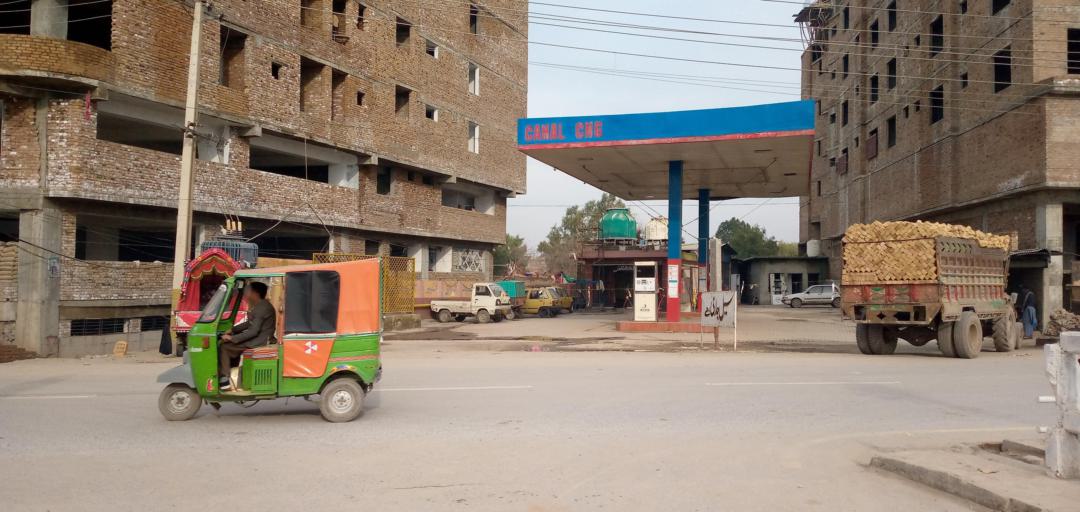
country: PK
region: Khyber Pakhtunkhwa
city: Peshawar
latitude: 34.0056
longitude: 71.4635
